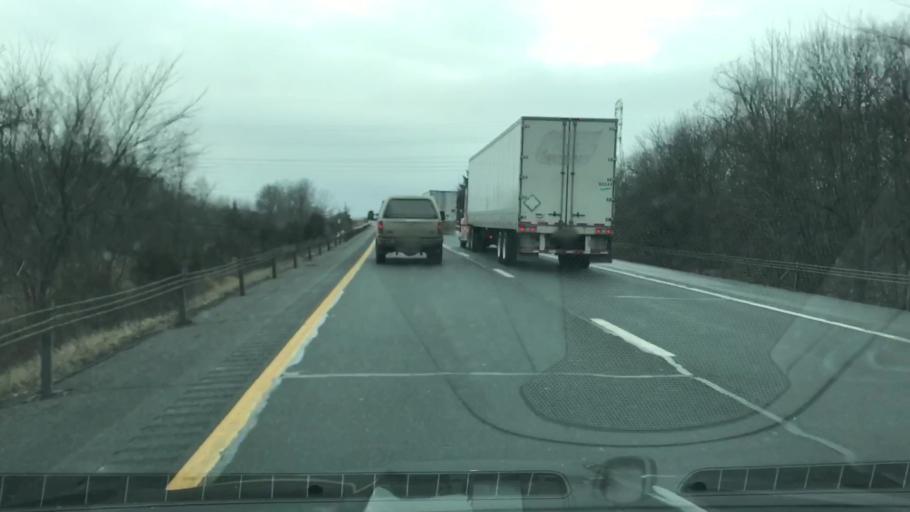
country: US
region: New York
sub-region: Orange County
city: Walden
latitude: 41.5179
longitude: -74.1796
